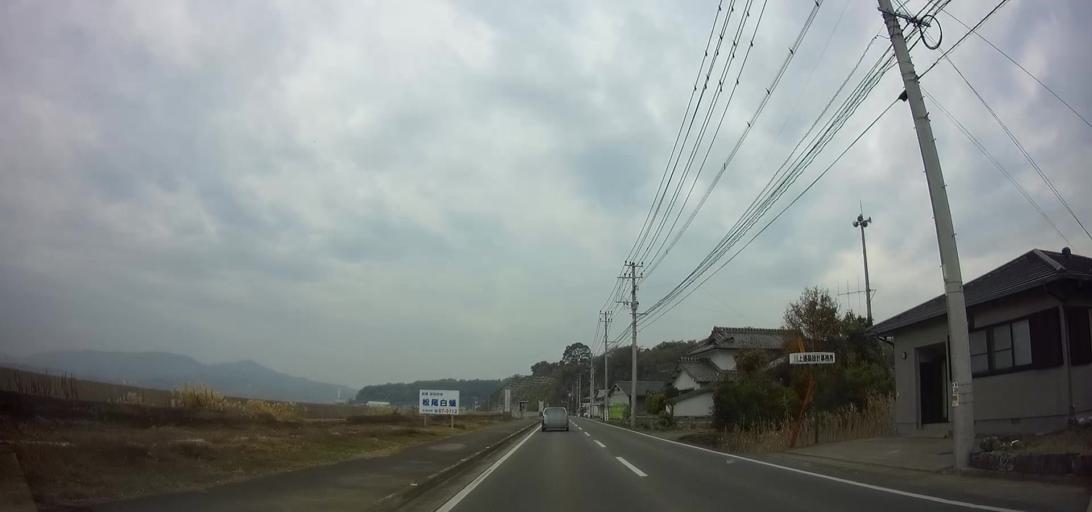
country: JP
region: Nagasaki
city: Shimabara
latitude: 32.6534
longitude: 130.2796
